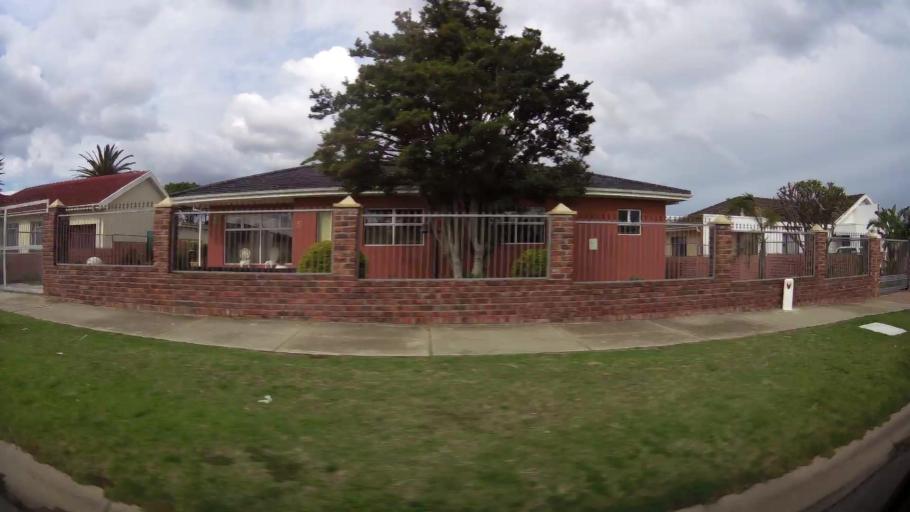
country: ZA
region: Eastern Cape
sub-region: Nelson Mandela Bay Metropolitan Municipality
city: Port Elizabeth
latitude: -33.9355
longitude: 25.5120
